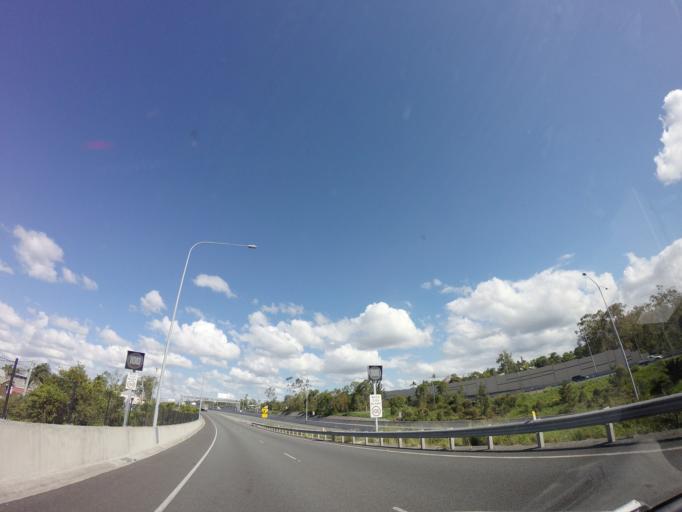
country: AU
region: Queensland
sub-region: Ipswich
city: Riverview
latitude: -27.5958
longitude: 152.8422
